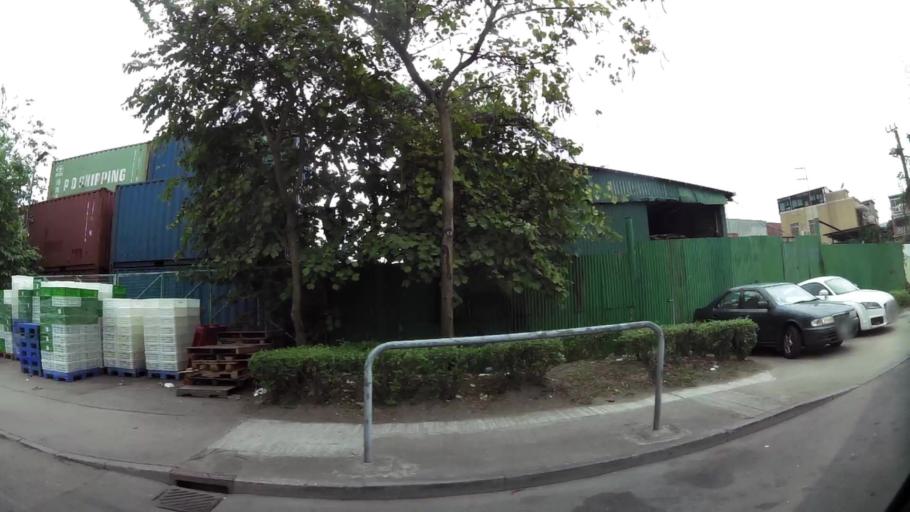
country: HK
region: Tuen Mun
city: Tuen Mun
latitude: 22.4238
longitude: 113.9920
